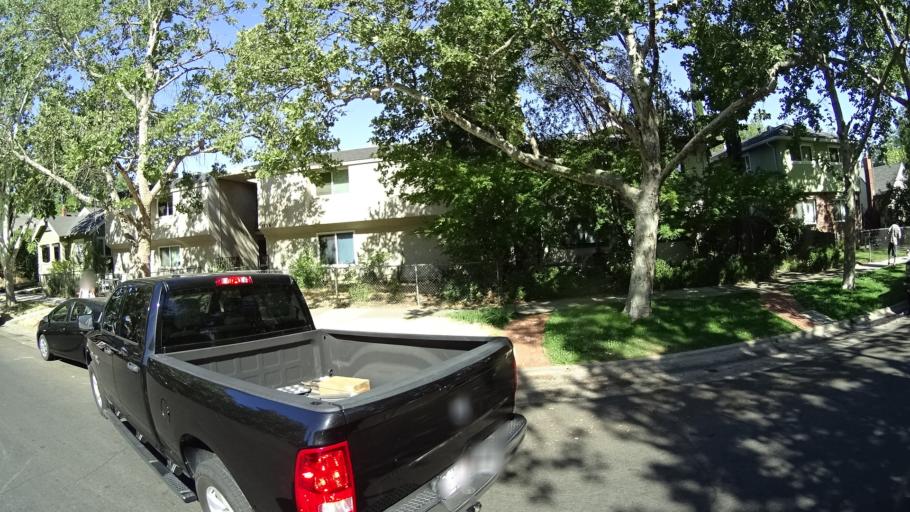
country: US
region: California
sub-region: Sacramento County
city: Sacramento
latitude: 38.5561
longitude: -121.4785
